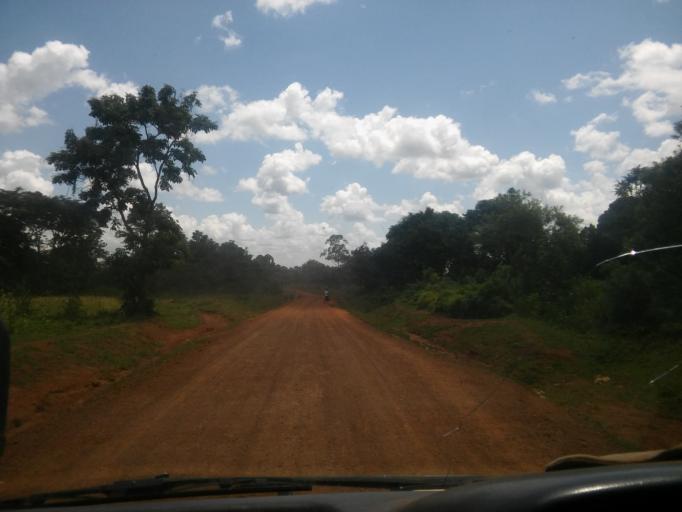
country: UG
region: Eastern Region
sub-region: Budaka District
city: Budaka
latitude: 1.1100
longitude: 33.9654
